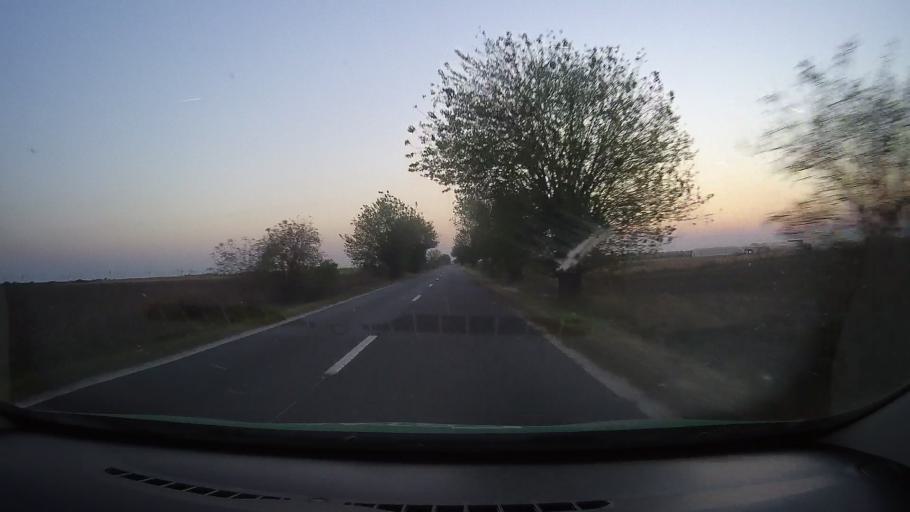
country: RO
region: Arad
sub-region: Comuna Zimandu Nou
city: Zimandu Nou
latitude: 46.2967
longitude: 21.4233
